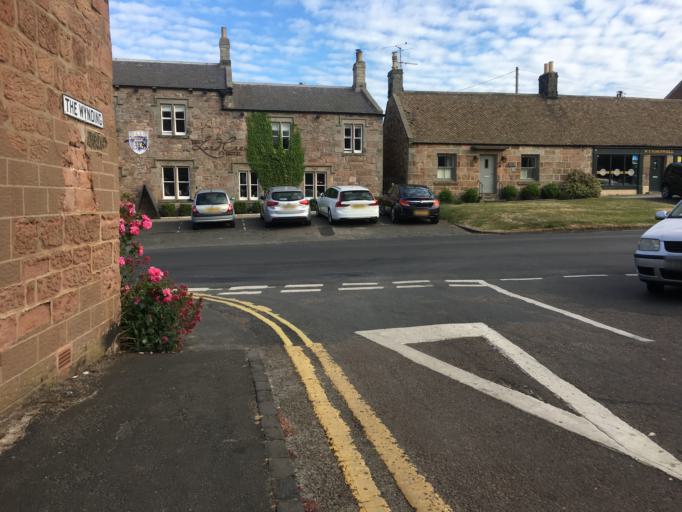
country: GB
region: England
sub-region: Northumberland
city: Bamburgh
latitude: 55.6079
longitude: -1.7144
